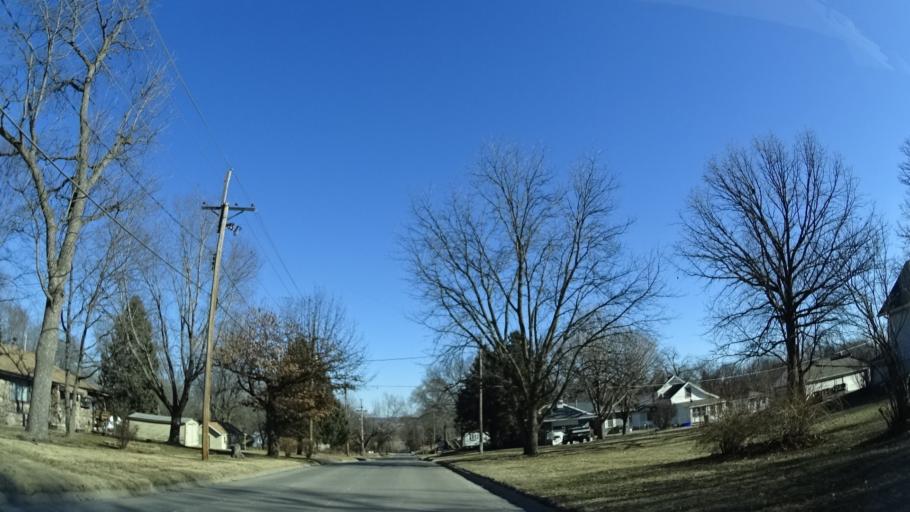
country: US
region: Nebraska
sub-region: Sarpy County
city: Bellevue
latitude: 41.1437
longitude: -95.8921
